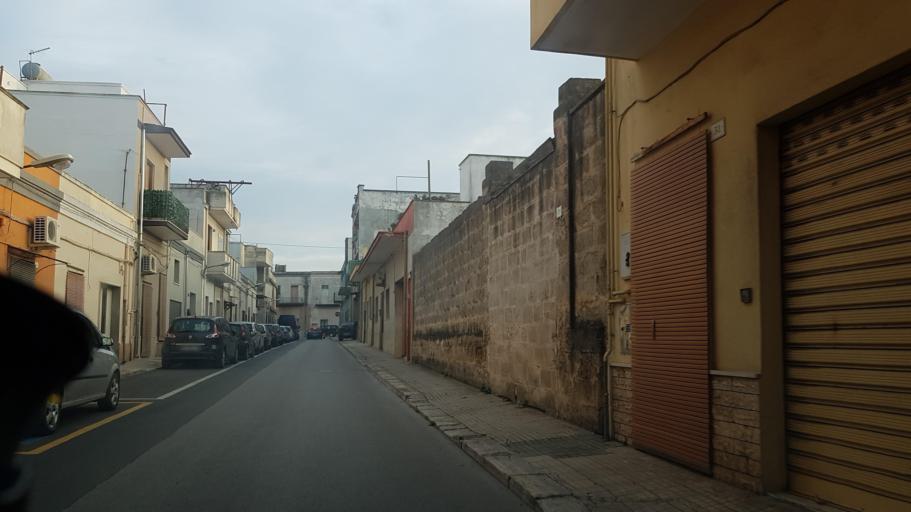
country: IT
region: Apulia
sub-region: Provincia di Brindisi
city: Latiano
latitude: 40.5541
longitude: 17.7243
